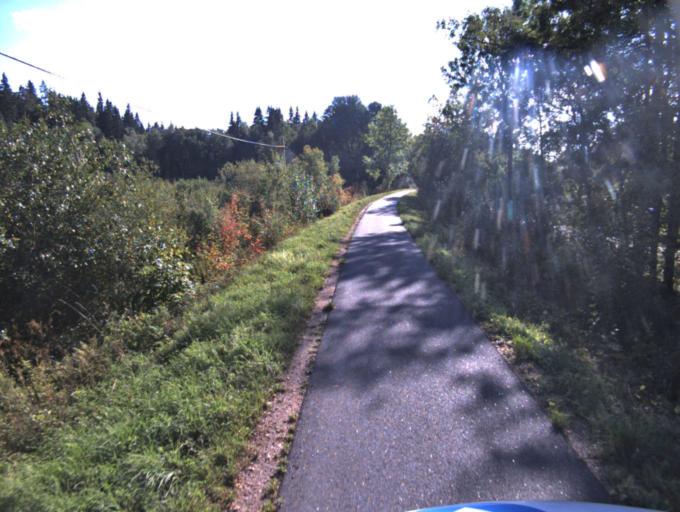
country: SE
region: Vaestra Goetaland
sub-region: Boras Kommun
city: Dalsjofors
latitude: 57.8168
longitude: 13.1476
